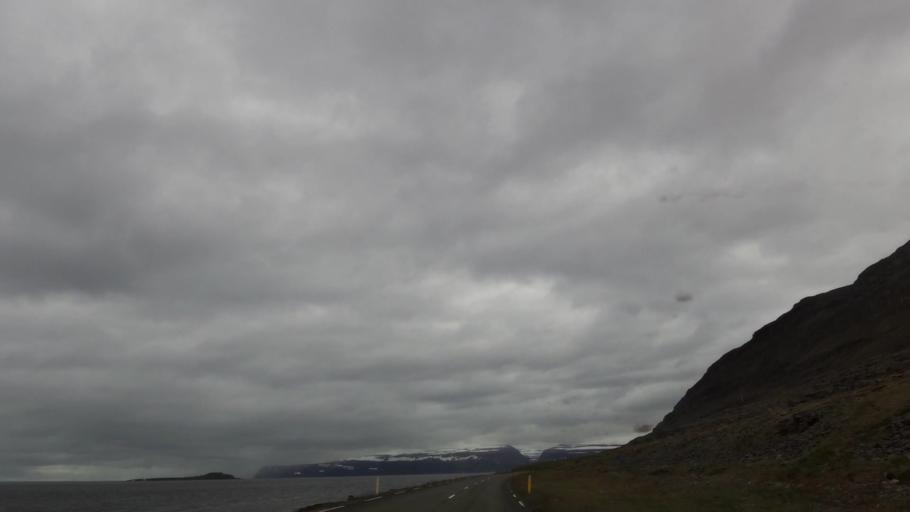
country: IS
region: Westfjords
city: Isafjoerdur
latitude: 66.0156
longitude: -22.7817
